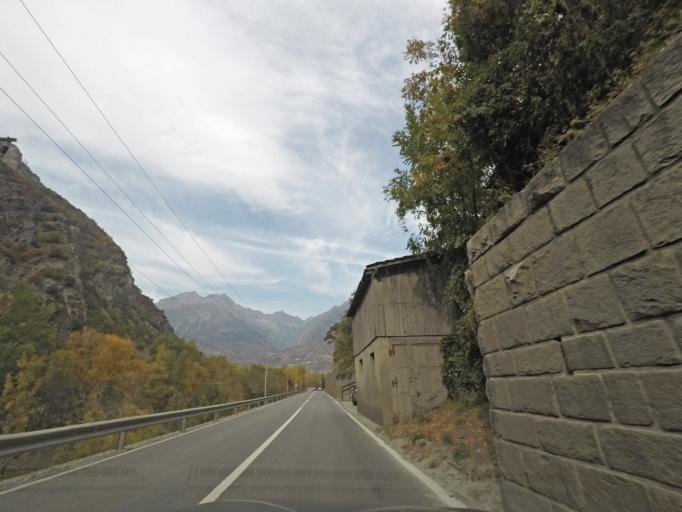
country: CH
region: Valais
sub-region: Visp District
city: Visp
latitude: 46.2734
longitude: 7.8819
